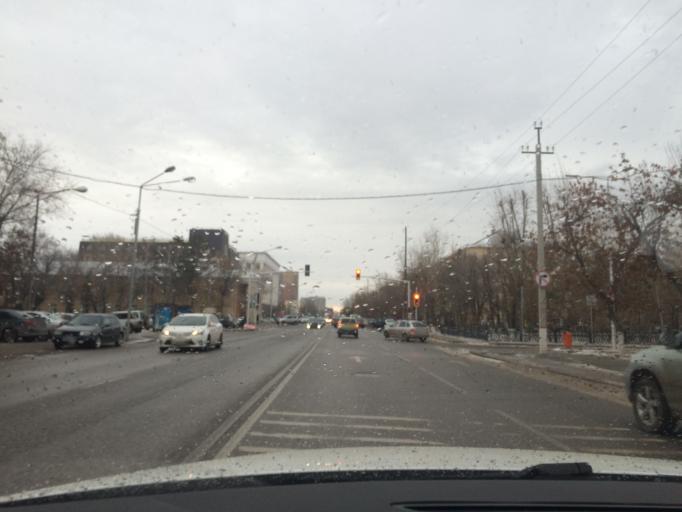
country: KZ
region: Astana Qalasy
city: Astana
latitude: 51.1836
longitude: 71.4220
